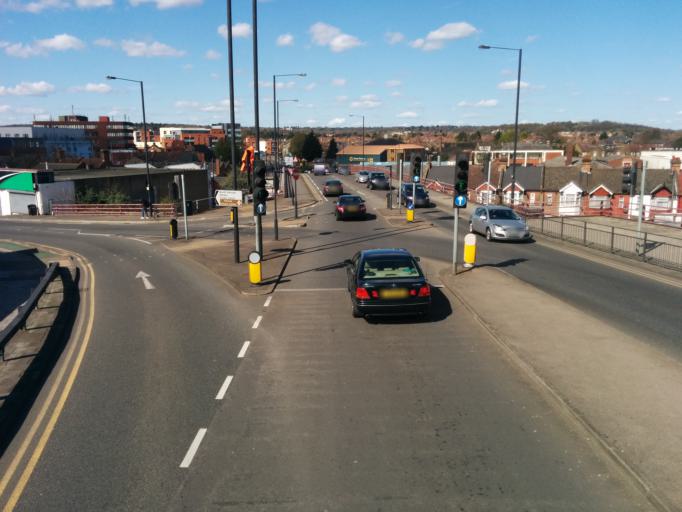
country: GB
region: England
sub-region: Greater London
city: Greenhill
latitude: 51.5916
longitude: -0.3333
